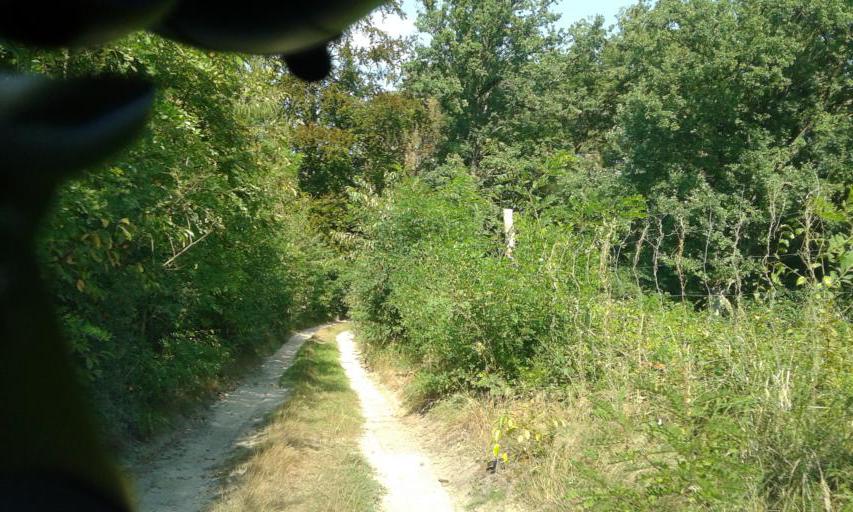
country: PL
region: West Pomeranian Voivodeship
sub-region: Powiat choszczenski
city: Krzecin
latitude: 53.0859
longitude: 15.4702
